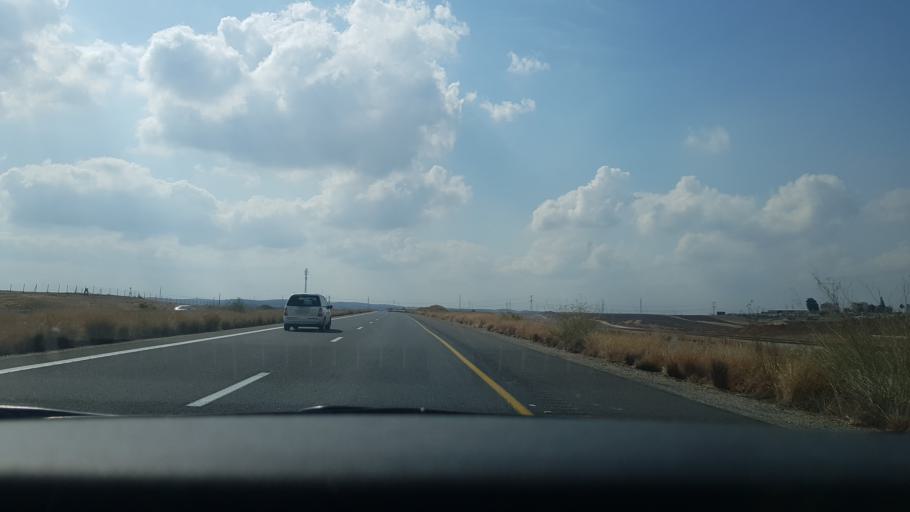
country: IL
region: Central District
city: Bene 'Ayish
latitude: 31.7261
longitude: 34.8207
